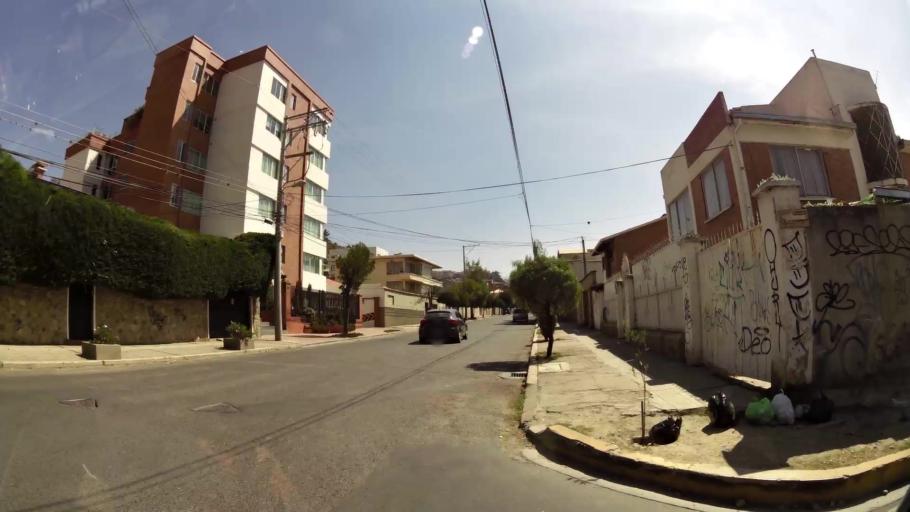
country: BO
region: La Paz
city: La Paz
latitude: -16.5414
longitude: -68.0957
